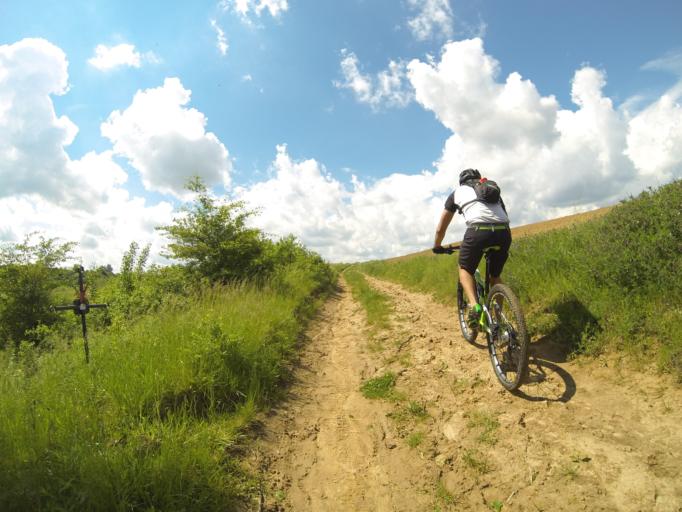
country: RO
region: Dolj
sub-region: Comuna Malu Mare
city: Preajba
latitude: 44.2676
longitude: 23.8523
